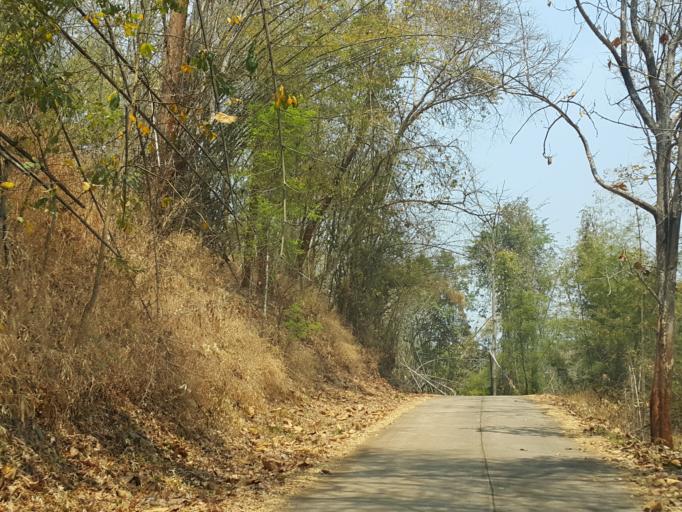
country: TH
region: Chiang Mai
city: Samoeng
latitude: 18.8023
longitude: 98.8069
